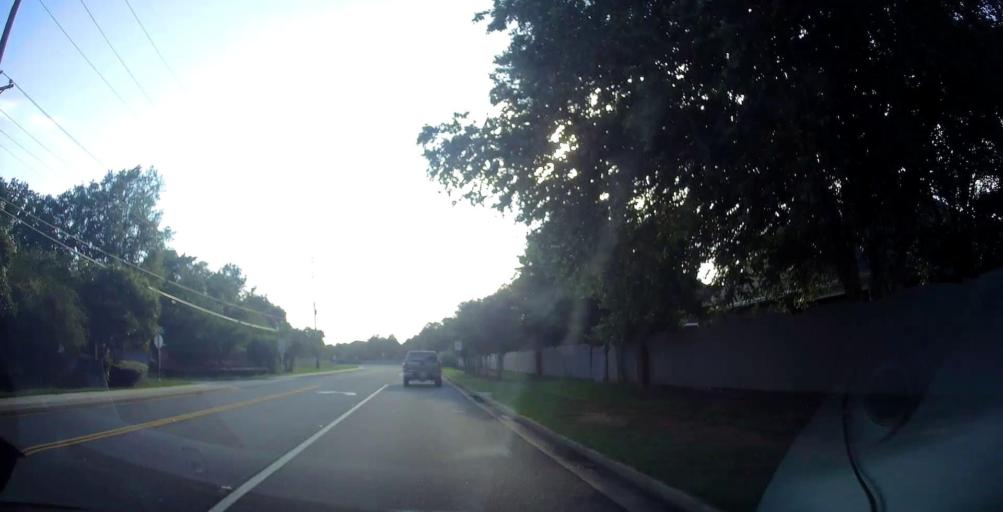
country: US
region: Georgia
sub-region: Houston County
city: Centerville
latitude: 32.6241
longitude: -83.6978
